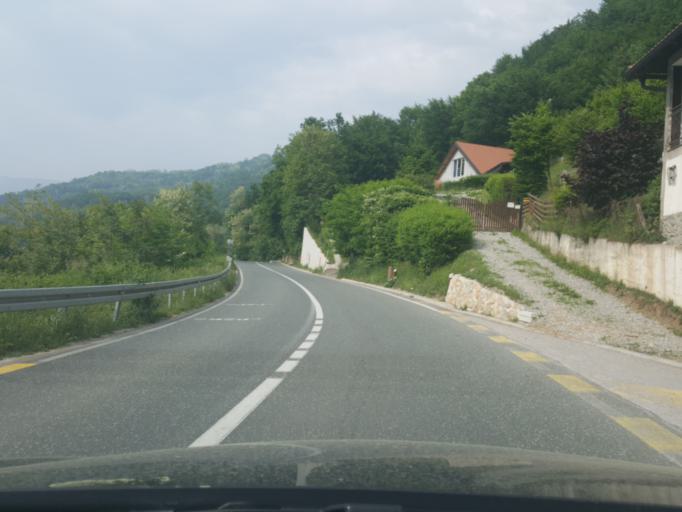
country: RS
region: Central Serbia
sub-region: Zlatiborski Okrug
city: Bajina Basta
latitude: 44.0158
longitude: 19.6219
